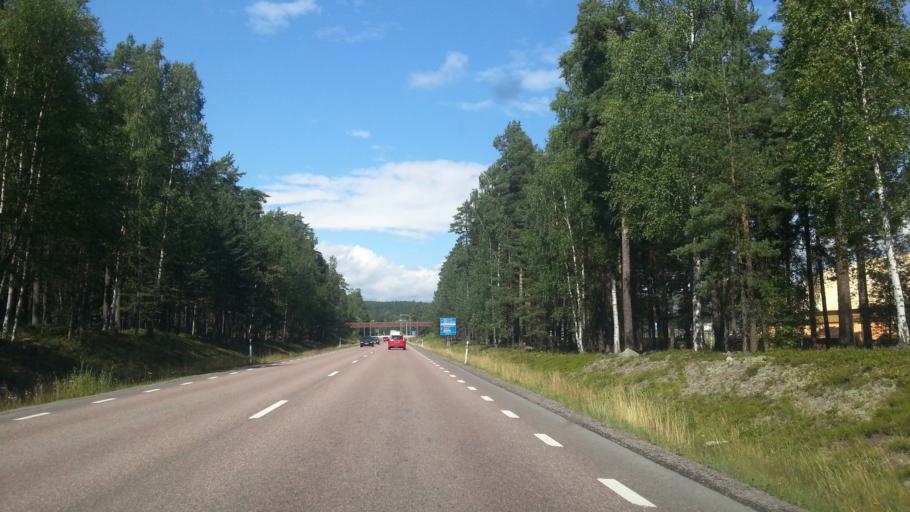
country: SE
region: Dalarna
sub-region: Faluns Kommun
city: Falun
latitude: 60.6154
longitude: 15.6502
